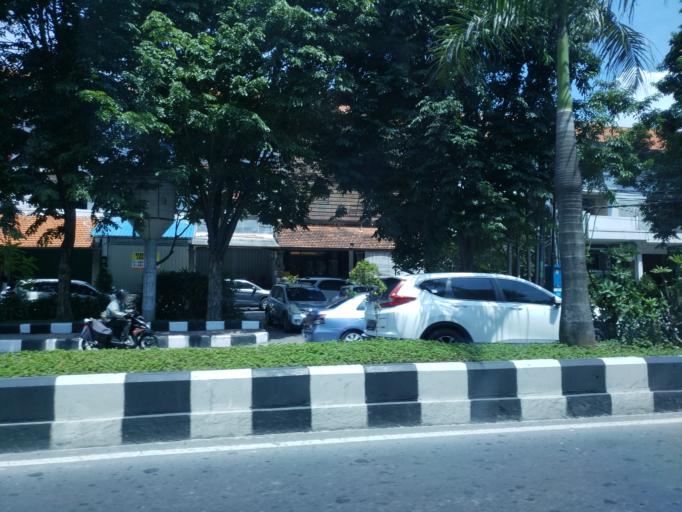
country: ID
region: Bali
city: Jabajero
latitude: -8.7381
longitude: 115.1799
